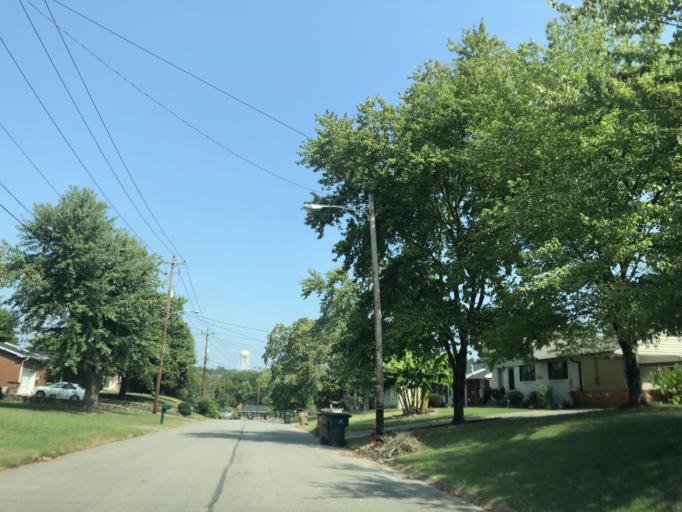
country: US
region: Tennessee
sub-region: Davidson County
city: Lakewood
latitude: 36.1562
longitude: -86.6435
